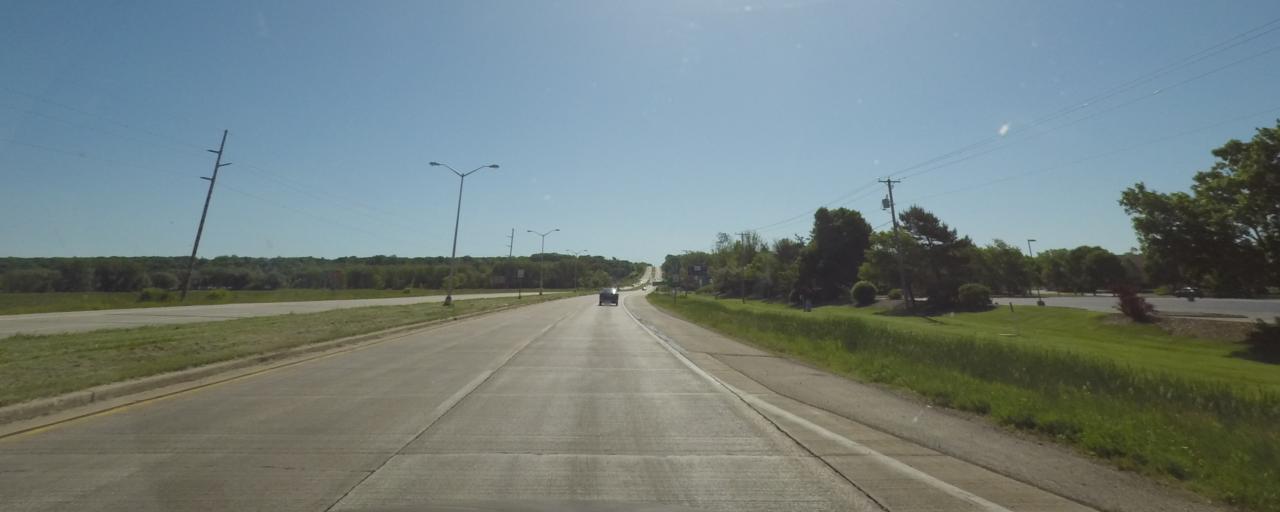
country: US
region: Wisconsin
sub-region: Fond du Lac County
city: Fond du Lac
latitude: 43.7836
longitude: -88.3995
